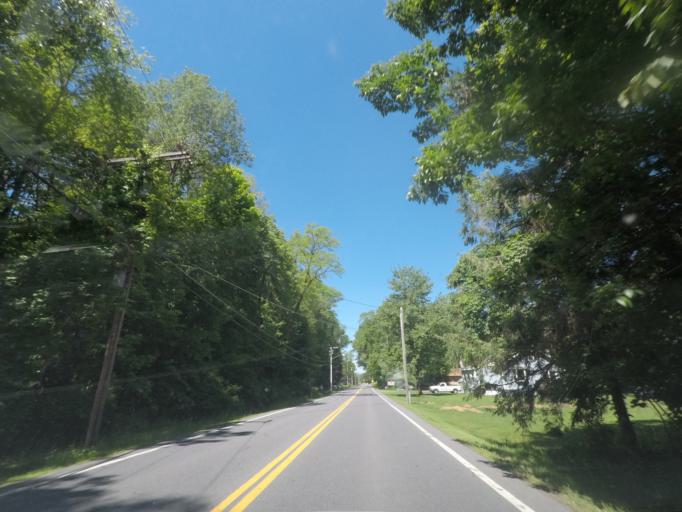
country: US
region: New York
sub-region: Saratoga County
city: Country Knolls
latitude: 42.8582
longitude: -73.8144
